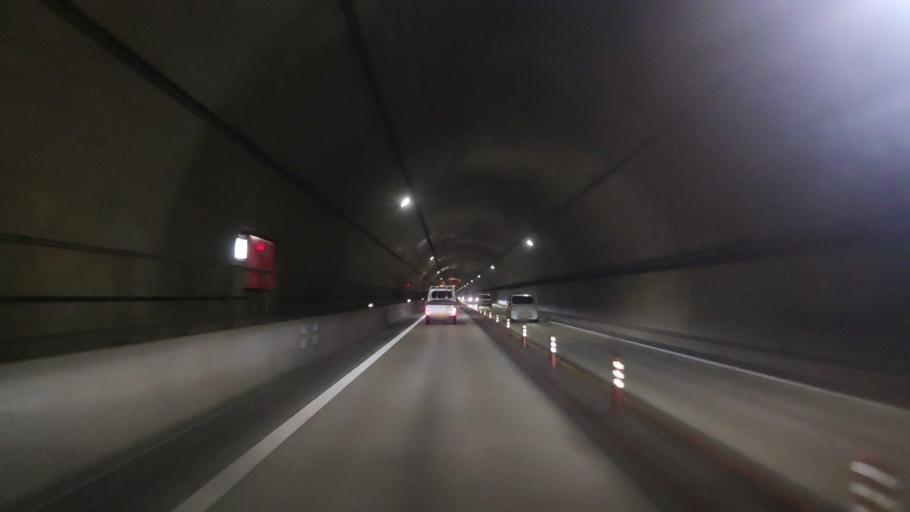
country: JP
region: Wakayama
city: Tanabe
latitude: 33.6173
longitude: 135.4221
